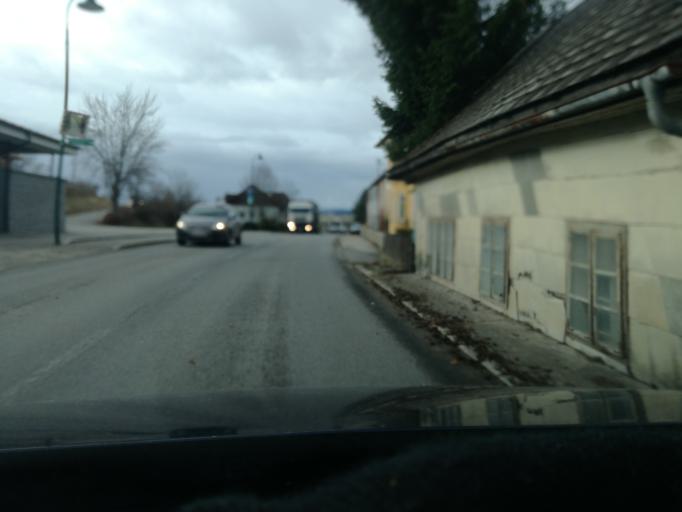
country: AT
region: Upper Austria
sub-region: Politischer Bezirk Vocklabruck
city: Frankenburg
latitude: 48.0718
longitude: 13.4929
